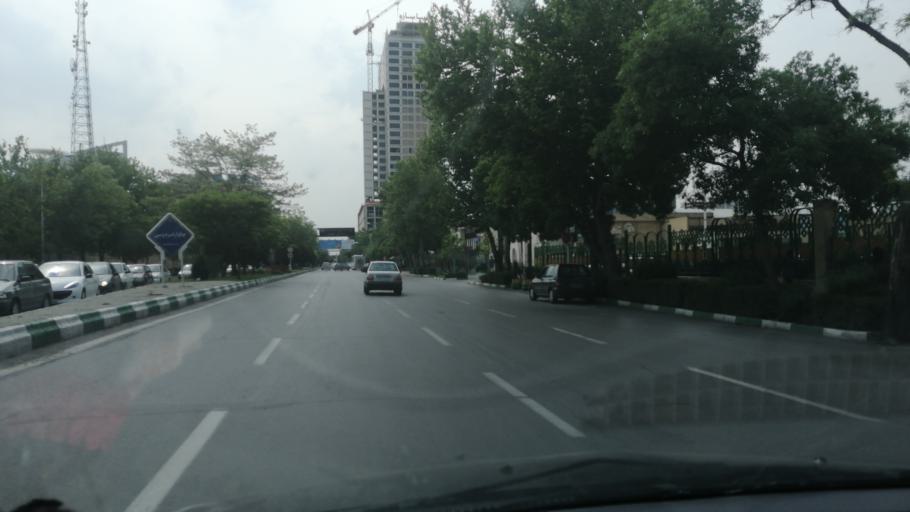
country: IR
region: Razavi Khorasan
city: Mashhad
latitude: 36.3242
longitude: 59.5696
